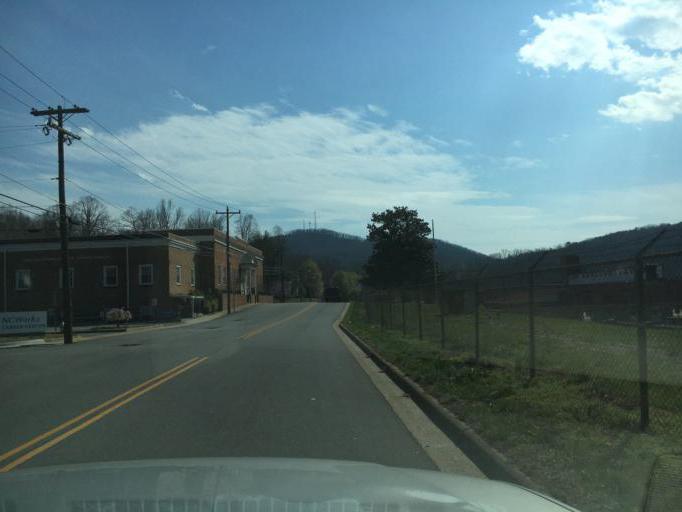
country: US
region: North Carolina
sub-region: McDowell County
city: Marion
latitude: 35.6802
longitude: -81.9919
